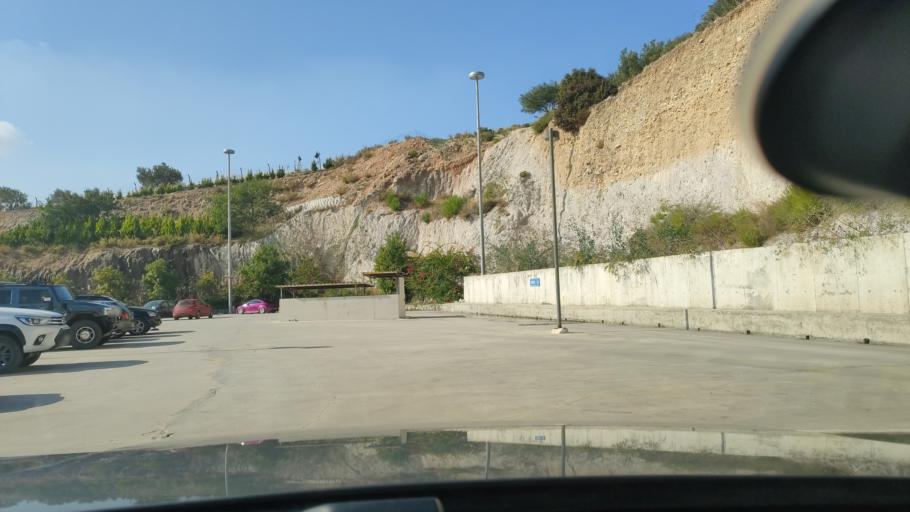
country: TR
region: Mugla
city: Ortakent
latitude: 37.0587
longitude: 27.3561
